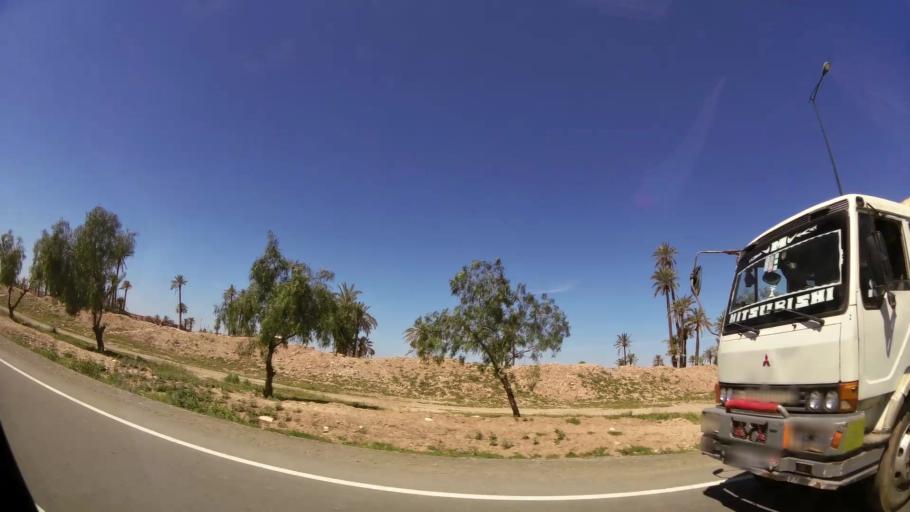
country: MA
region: Marrakech-Tensift-Al Haouz
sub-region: Marrakech
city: Marrakesh
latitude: 31.6688
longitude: -7.9905
